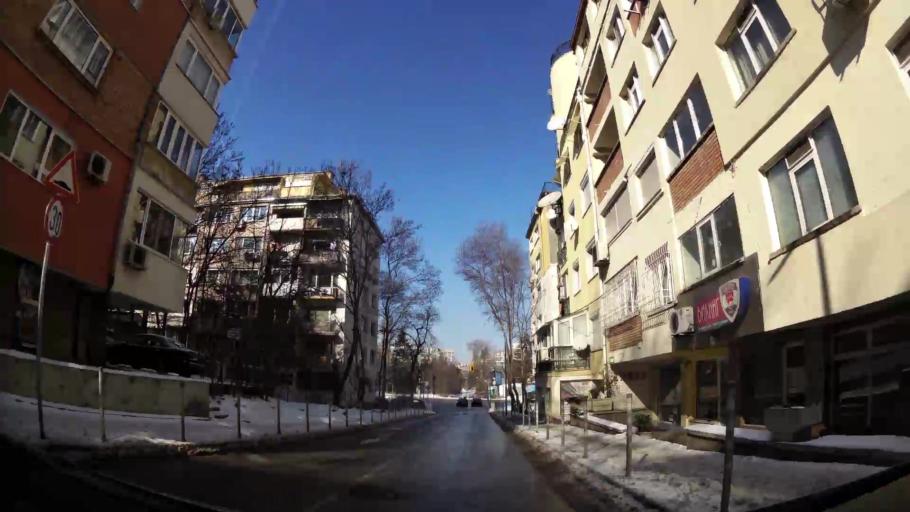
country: BG
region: Sofia-Capital
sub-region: Stolichna Obshtina
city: Sofia
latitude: 42.6735
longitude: 23.3126
